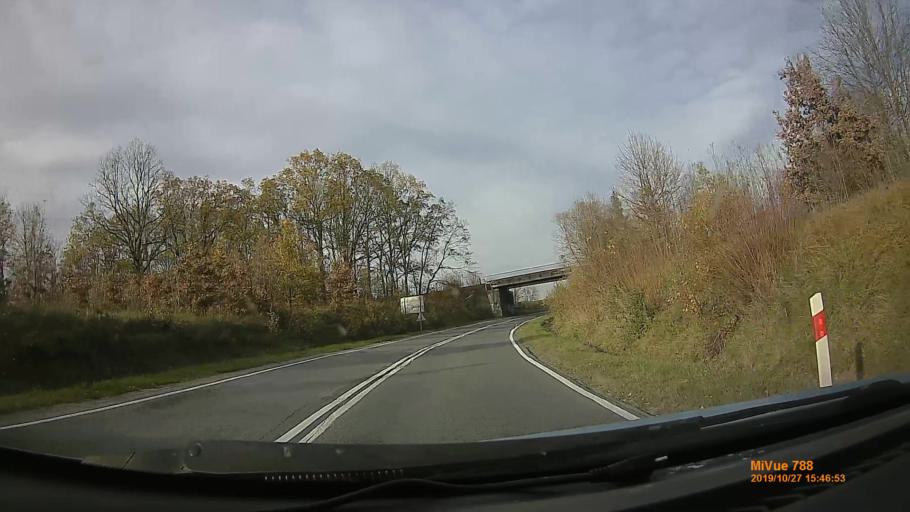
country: PL
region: Lower Silesian Voivodeship
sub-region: Powiat klodzki
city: Bozkow
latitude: 50.4849
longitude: 16.5824
